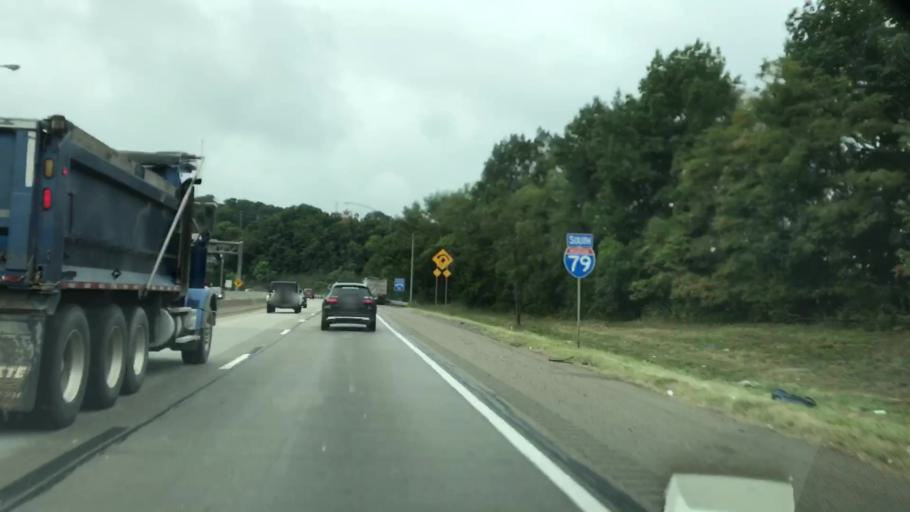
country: US
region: Pennsylvania
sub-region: Allegheny County
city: Coraopolis
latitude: 40.5106
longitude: -80.1364
